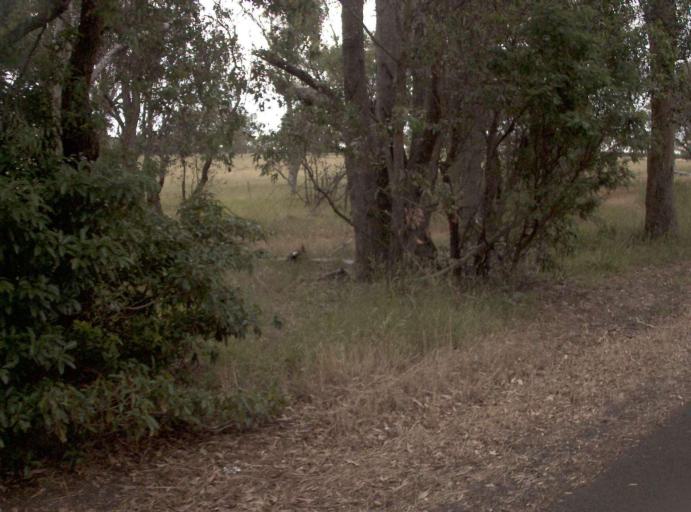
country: AU
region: Victoria
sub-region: Wellington
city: Sale
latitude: -38.3730
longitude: 146.9853
